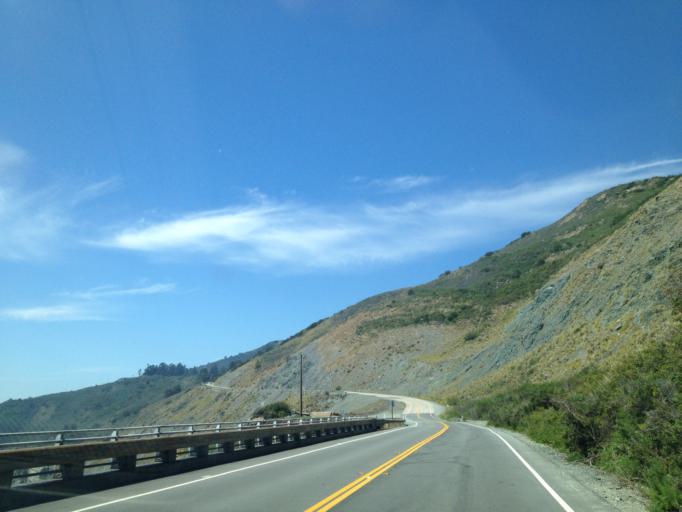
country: US
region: California
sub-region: Monterey County
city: Greenfield
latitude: 36.0130
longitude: -121.5265
